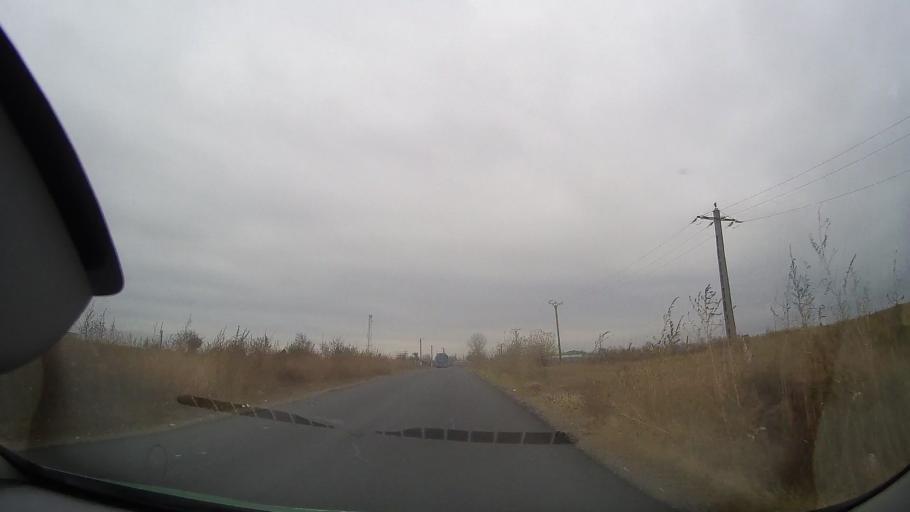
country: RO
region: Braila
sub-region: Comuna Ciresu
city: Ciresu
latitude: 44.9434
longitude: 27.3365
